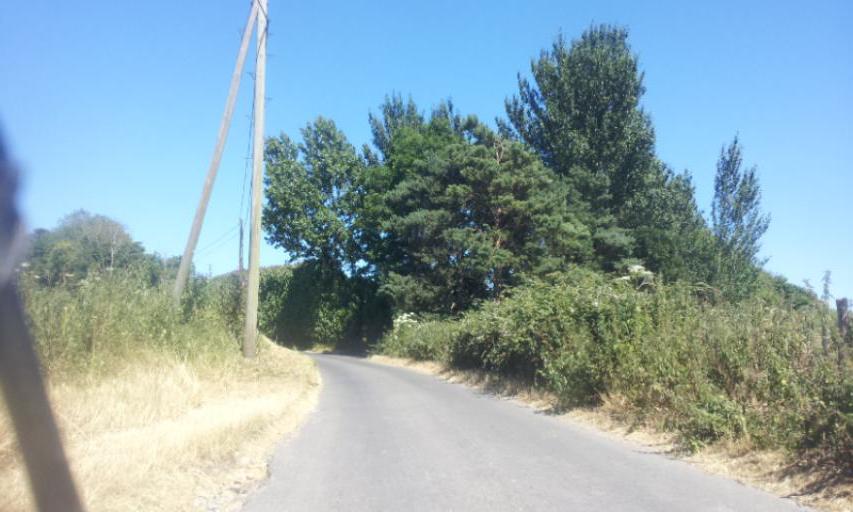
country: GB
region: England
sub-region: Kent
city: Teynham
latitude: 51.3468
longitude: 0.7786
